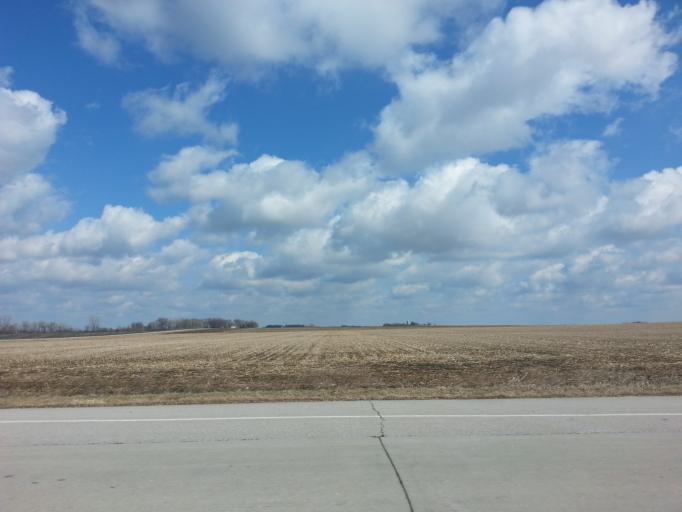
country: US
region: Minnesota
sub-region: Dodge County
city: Dodge Center
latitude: 44.1015
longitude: -92.8996
